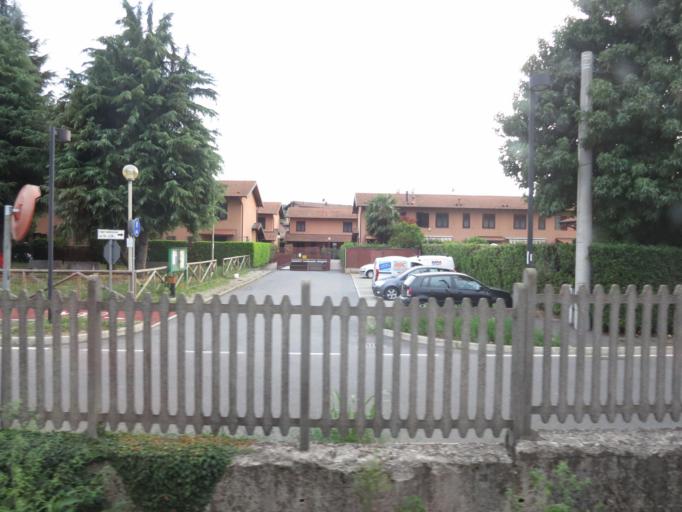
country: IT
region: Lombardy
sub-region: Provincia di Como
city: Novedrate
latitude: 45.6920
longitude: 9.1160
